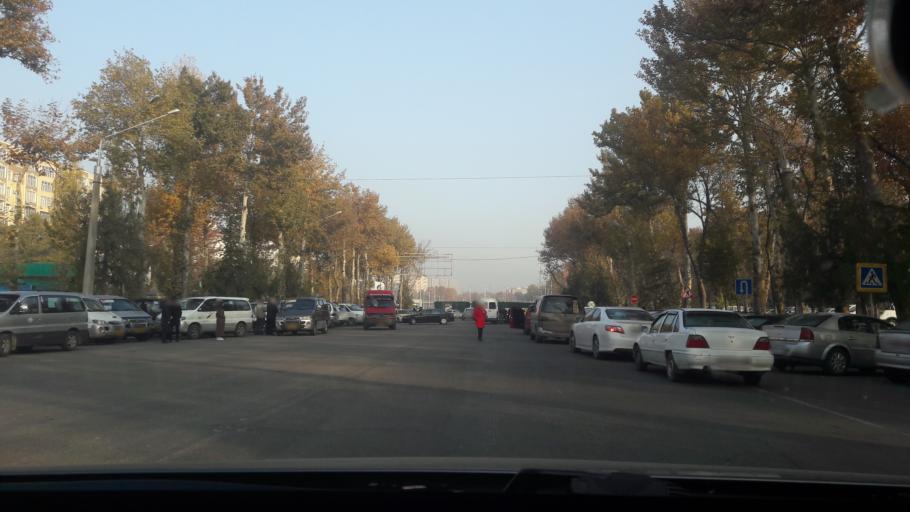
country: TJ
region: Dushanbe
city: Dushanbe
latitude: 38.5800
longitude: 68.7551
